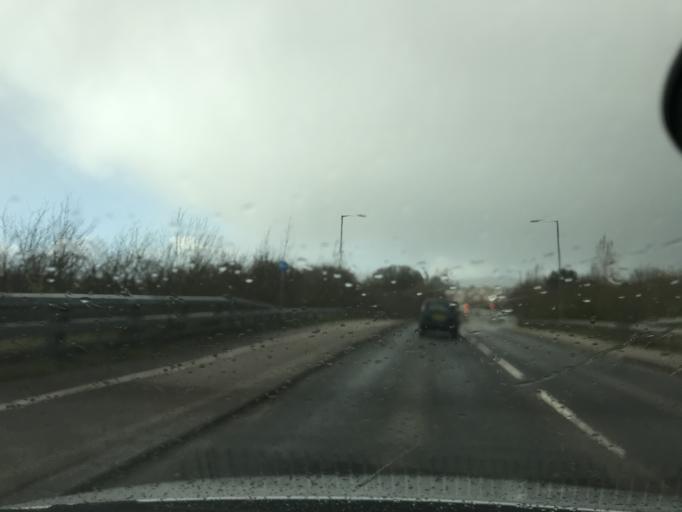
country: GB
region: England
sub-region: Somerset
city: Taunton
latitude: 51.0252
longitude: -3.1331
